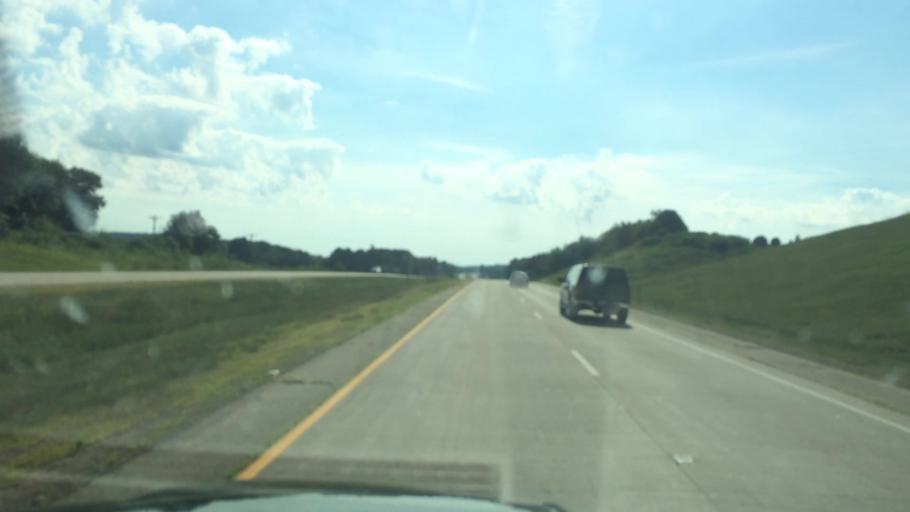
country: US
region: Wisconsin
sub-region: Shawano County
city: Wittenberg
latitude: 44.8259
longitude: -89.1052
